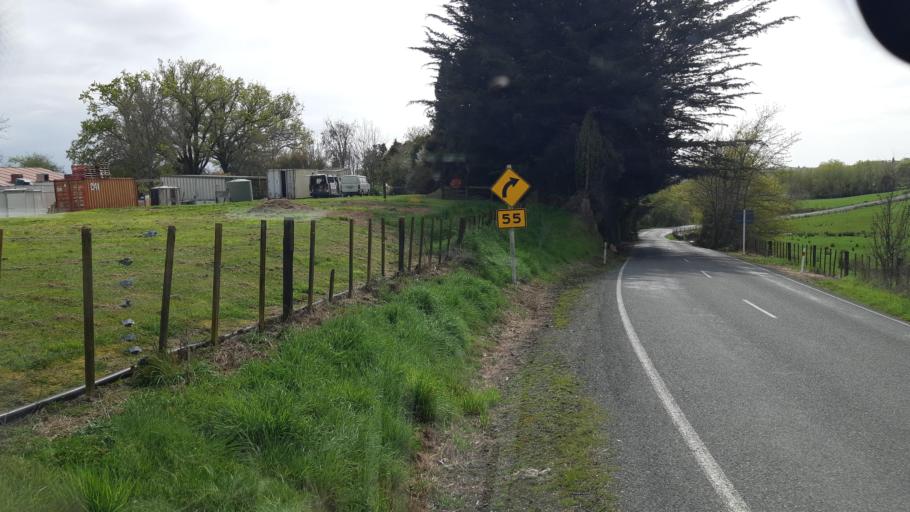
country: NZ
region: Tasman
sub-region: Tasman District
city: Mapua
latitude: -41.2517
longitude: 172.9828
